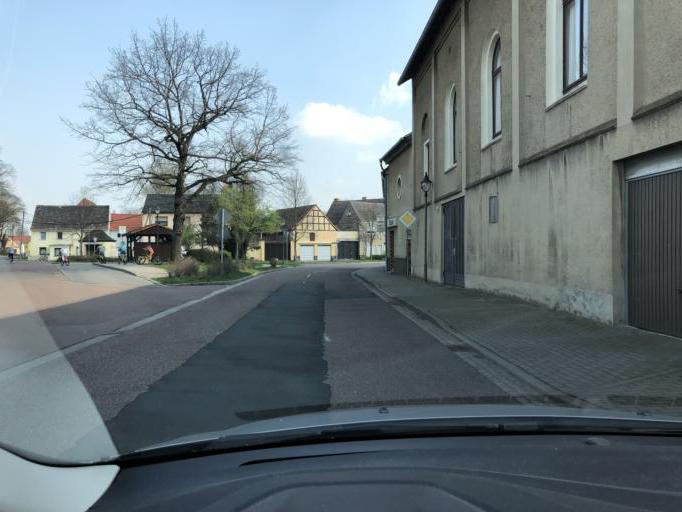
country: DE
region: Saxony-Anhalt
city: Oppin
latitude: 51.5703
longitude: 12.0510
